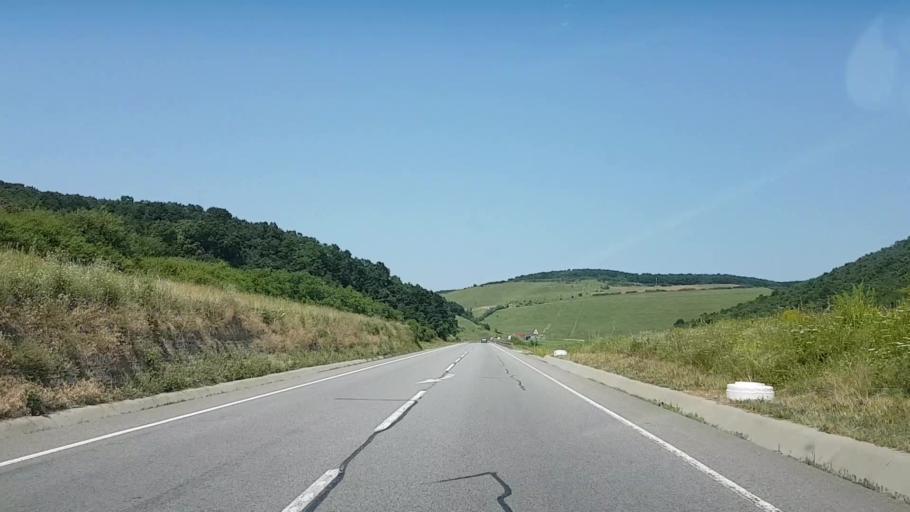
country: RO
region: Cluj
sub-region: Comuna Feleacu
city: Gheorghieni
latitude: 46.7356
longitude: 23.7066
